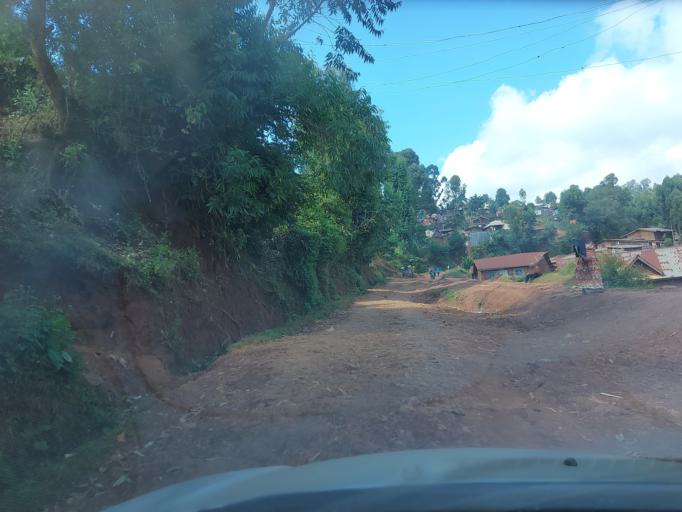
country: CD
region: South Kivu
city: Bukavu
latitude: -2.5123
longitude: 28.8399
